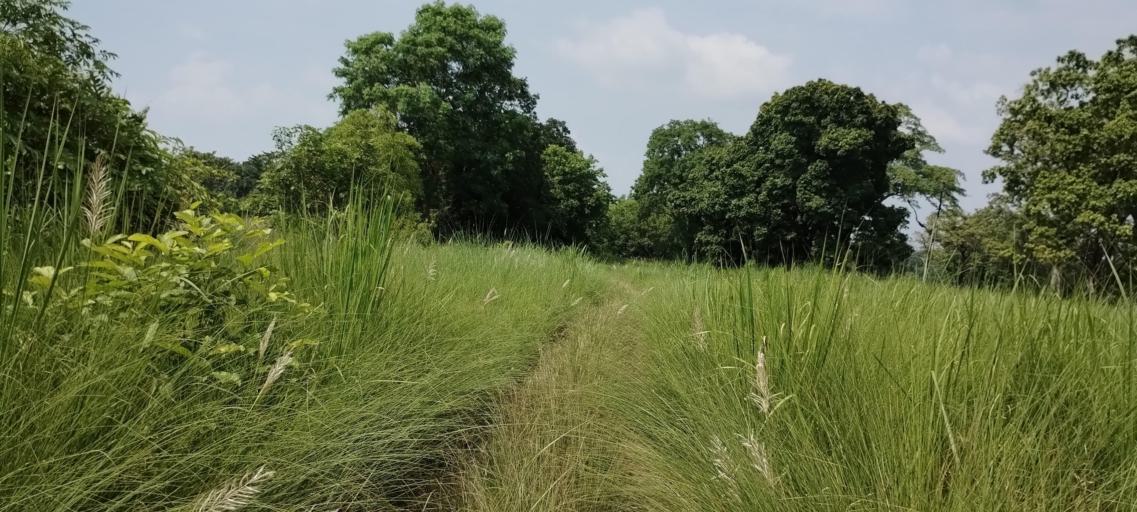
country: NP
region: Far Western
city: Tikapur
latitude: 28.5079
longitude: 81.2476
